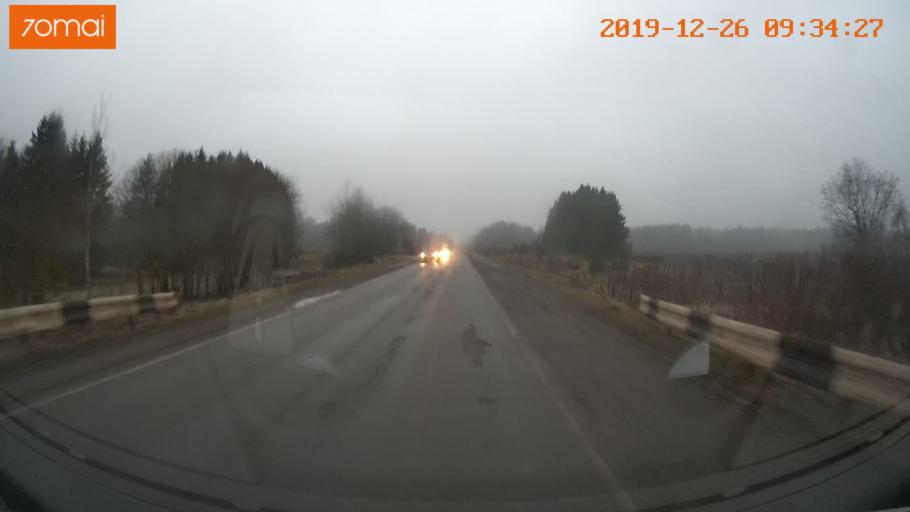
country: RU
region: Vologda
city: Vologda
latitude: 59.1019
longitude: 40.0860
